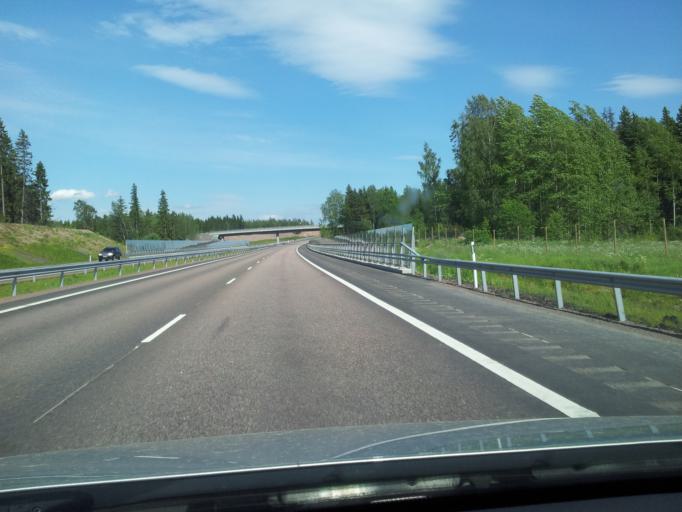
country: FI
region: Uusimaa
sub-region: Loviisa
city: Lovisa
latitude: 60.4881
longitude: 26.3074
